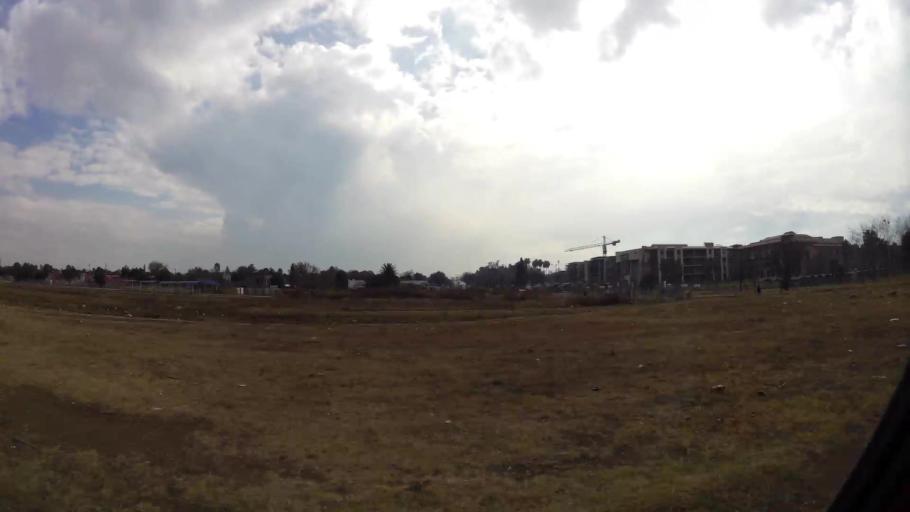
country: ZA
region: Gauteng
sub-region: Sedibeng District Municipality
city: Vanderbijlpark
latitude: -26.7135
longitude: 27.8611
